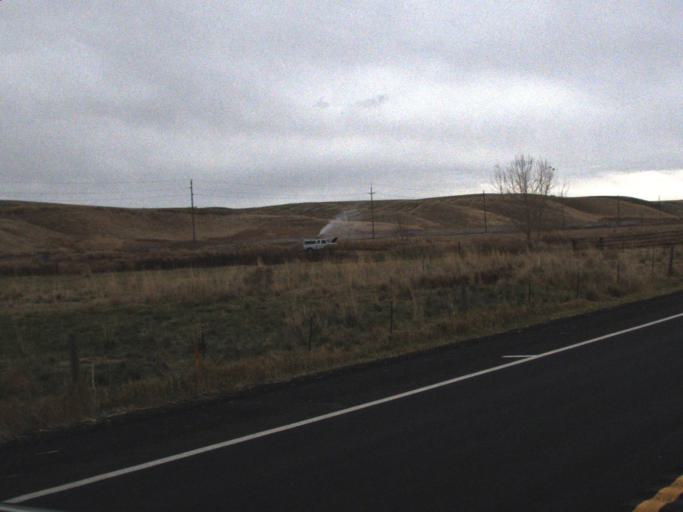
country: US
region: Washington
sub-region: Walla Walla County
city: Garrett
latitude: 46.0542
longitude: -118.5664
